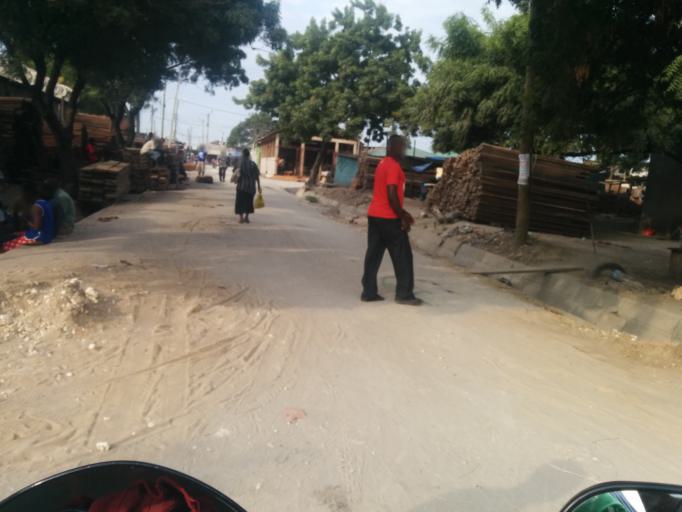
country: TZ
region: Dar es Salaam
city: Dar es Salaam
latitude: -6.8374
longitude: 39.2716
